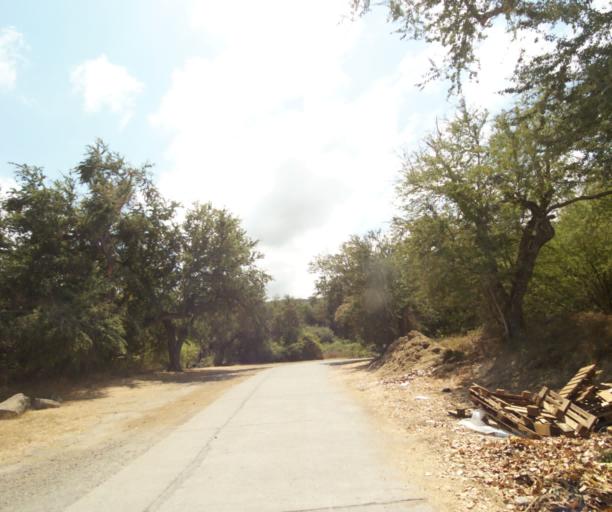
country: RE
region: Reunion
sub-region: Reunion
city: Trois-Bassins
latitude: -21.0912
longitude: 55.2371
